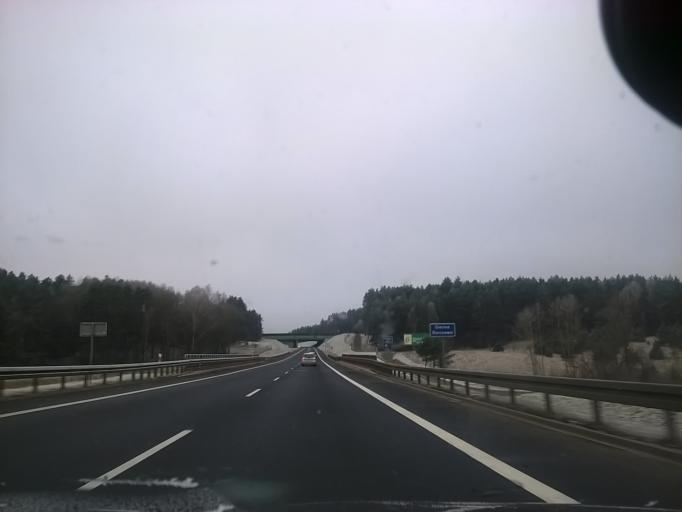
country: PL
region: Warmian-Masurian Voivodeship
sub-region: Powiat olsztynski
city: Czerwonka
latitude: 53.8271
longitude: 20.8483
